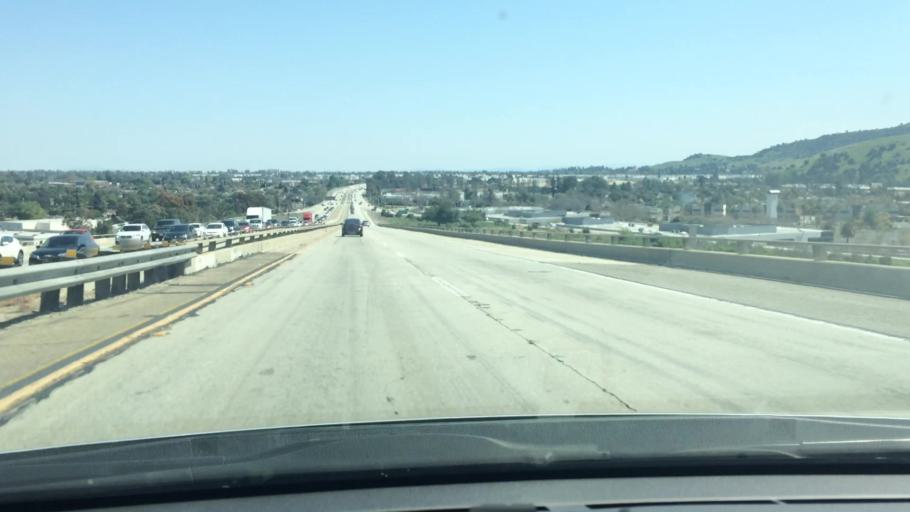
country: US
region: California
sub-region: Los Angeles County
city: San Dimas
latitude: 34.0677
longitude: -117.8053
